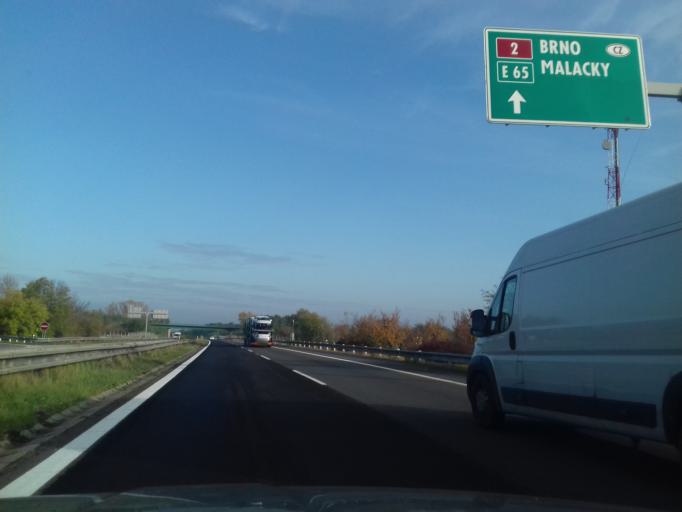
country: SK
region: Bratislavsky
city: Stupava
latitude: 48.3273
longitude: 17.0239
